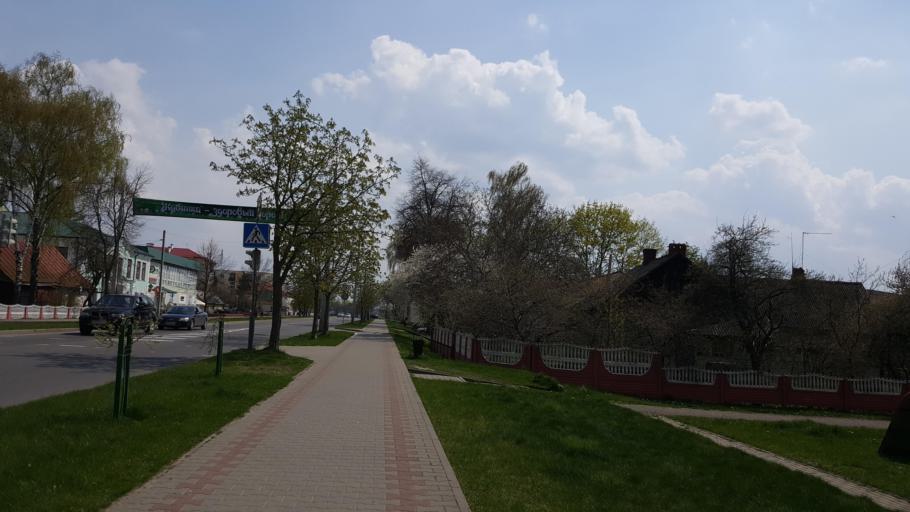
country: BY
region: Brest
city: Zhabinka
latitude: 52.1954
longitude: 24.0152
